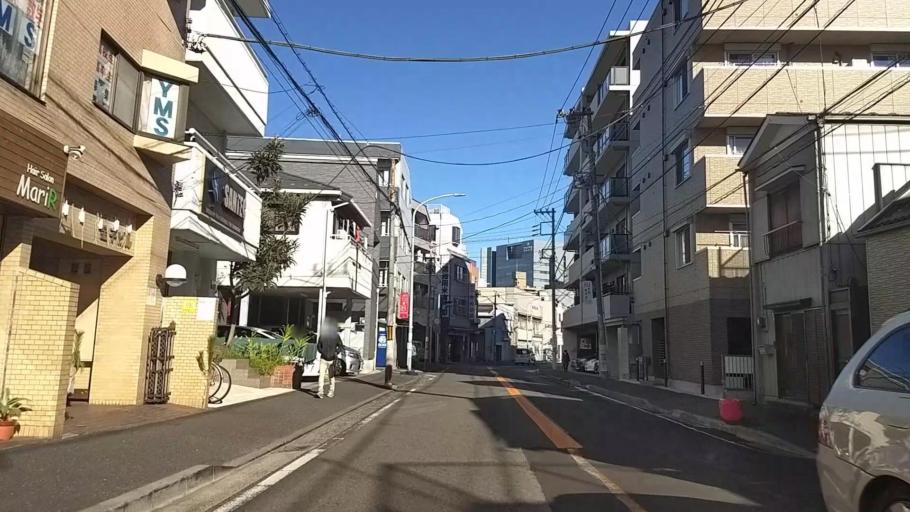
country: JP
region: Kanagawa
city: Yokohama
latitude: 35.4539
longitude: 139.6239
